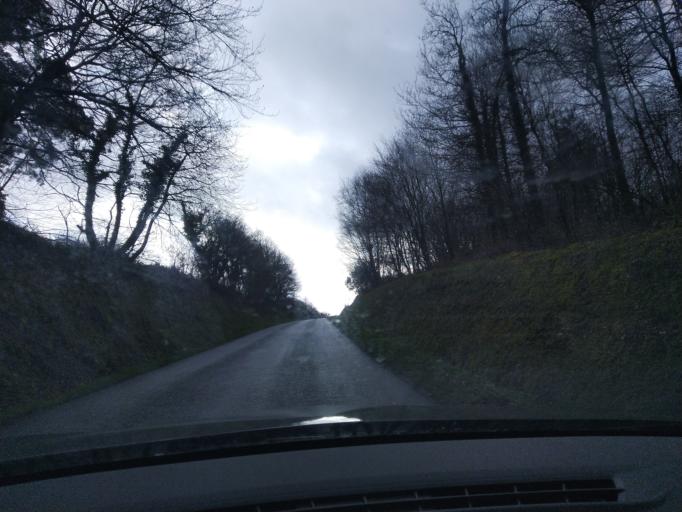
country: FR
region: Brittany
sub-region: Departement du Finistere
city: Guerlesquin
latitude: 48.4999
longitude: -3.5869
